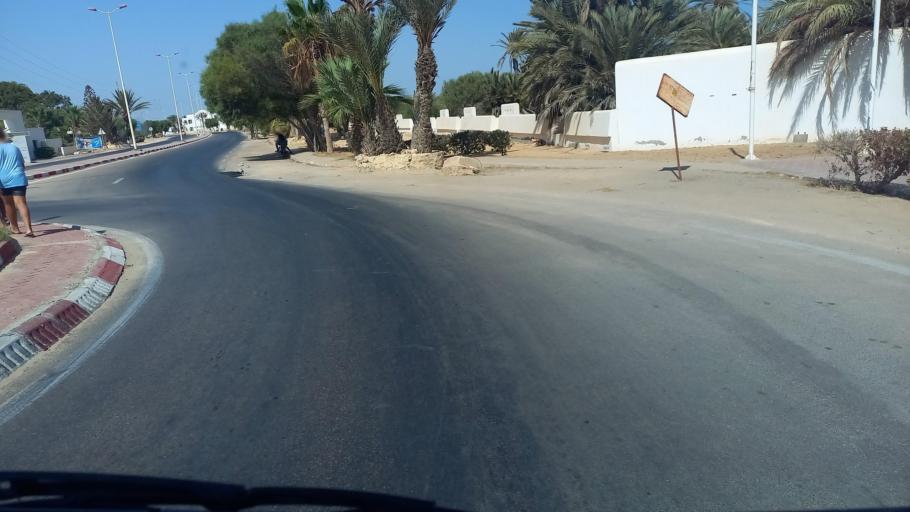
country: TN
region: Madanin
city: Midoun
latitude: 33.8271
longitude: 11.0316
